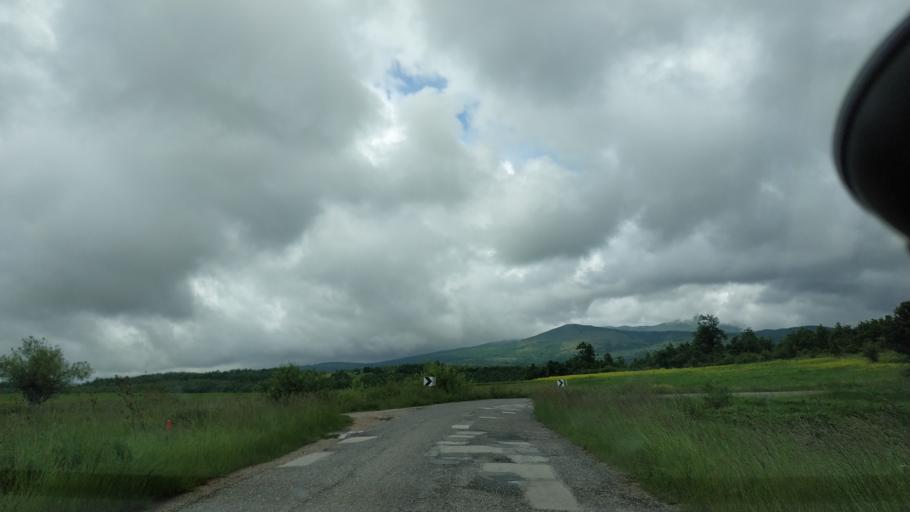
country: RS
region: Central Serbia
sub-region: Zajecarski Okrug
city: Soko Banja
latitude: 43.7017
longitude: 21.9355
